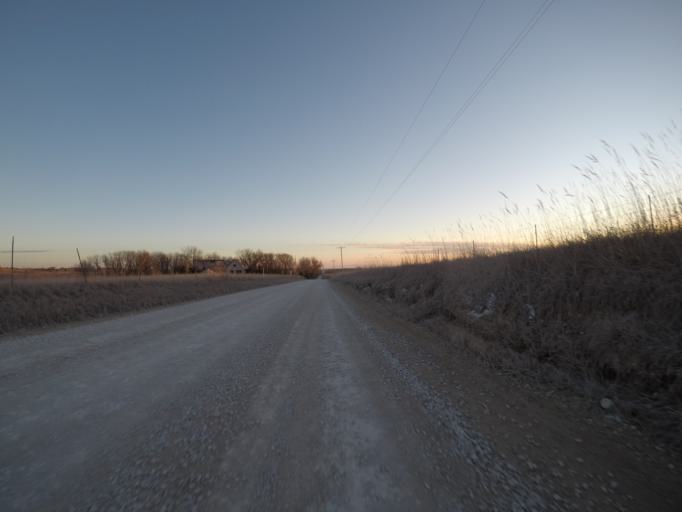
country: US
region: Kansas
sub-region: Riley County
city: Manhattan
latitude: 39.2614
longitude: -96.4827
